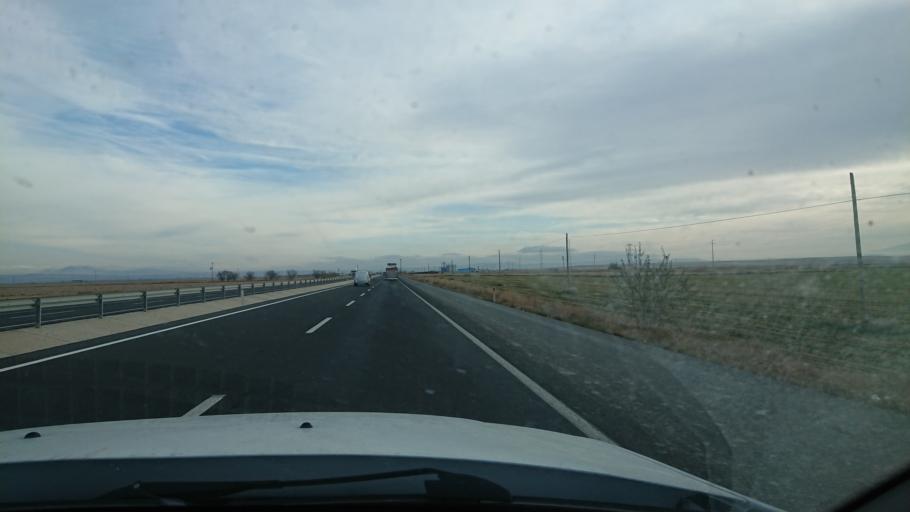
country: TR
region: Aksaray
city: Yesilova
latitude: 38.3147
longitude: 33.8469
